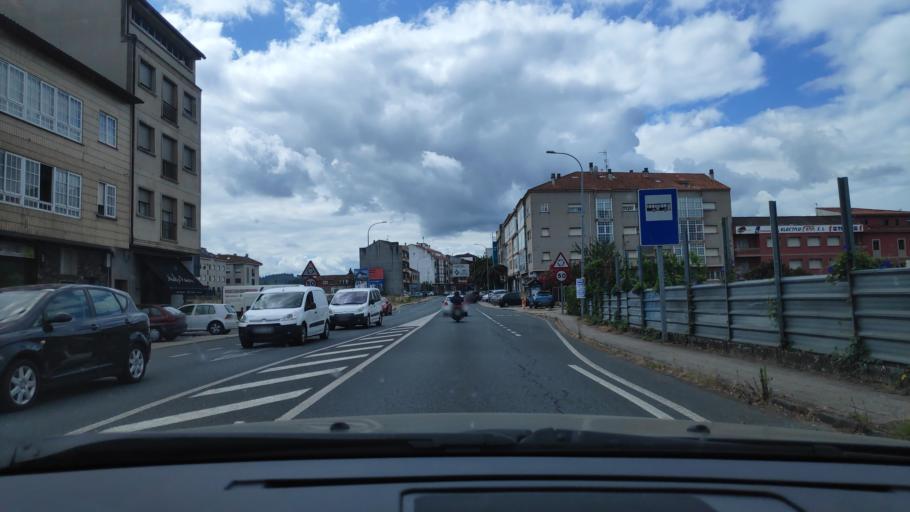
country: ES
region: Galicia
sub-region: Provincia da Coruna
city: Padron
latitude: 42.7188
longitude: -8.6511
